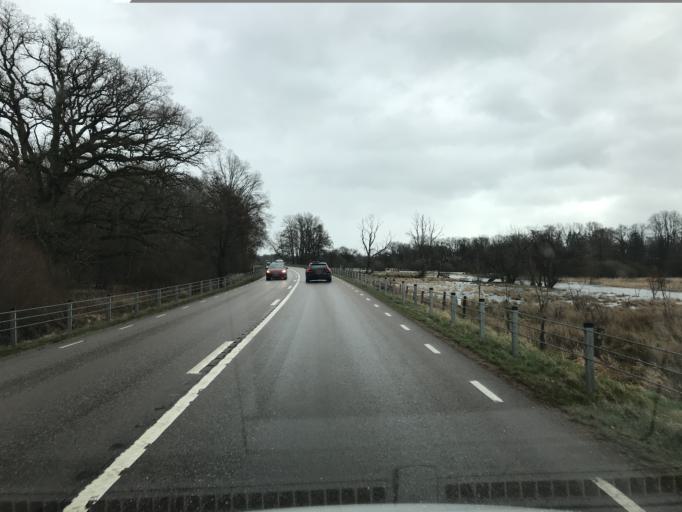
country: SE
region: Skane
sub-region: Klippans Kommun
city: Ljungbyhed
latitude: 56.0889
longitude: 13.2266
